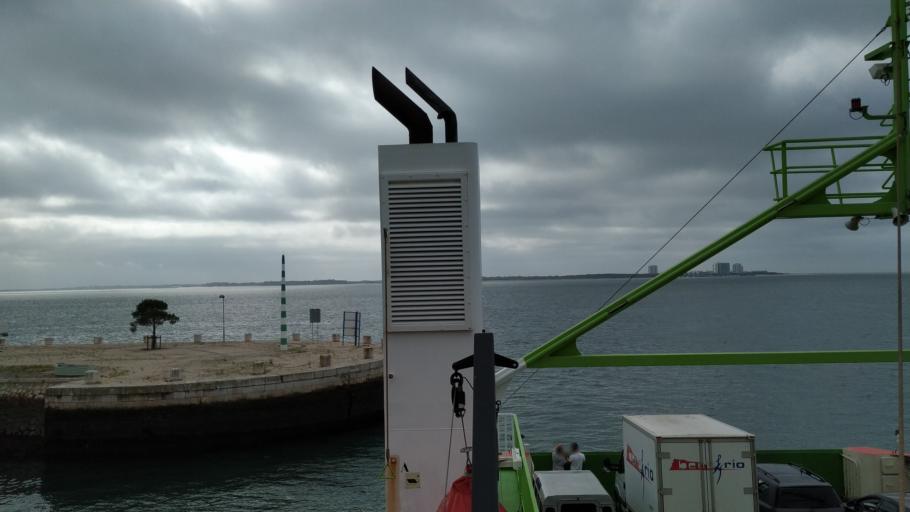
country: PT
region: Setubal
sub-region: Setubal
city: Setubal
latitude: 38.5209
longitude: -8.8853
